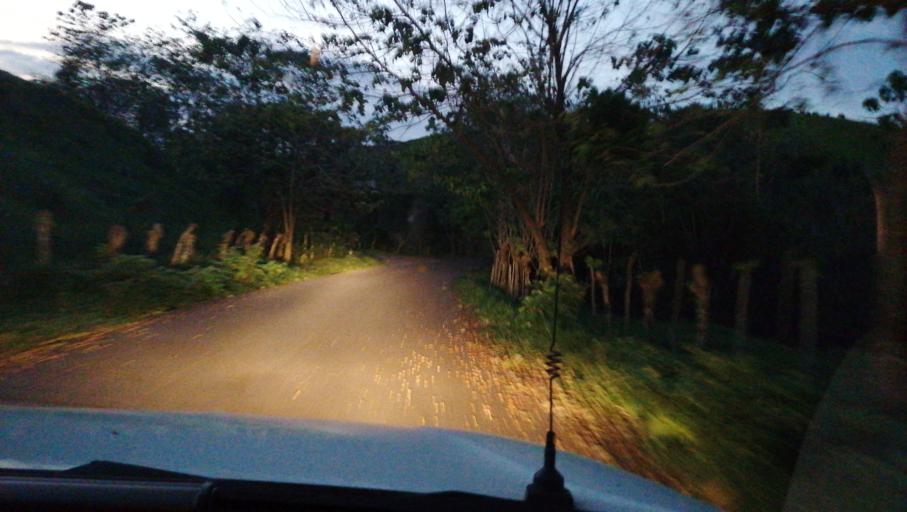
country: MX
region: Chiapas
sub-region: Ostuacan
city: Nuevo Juan del Grijalva
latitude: 17.4810
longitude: -93.3492
